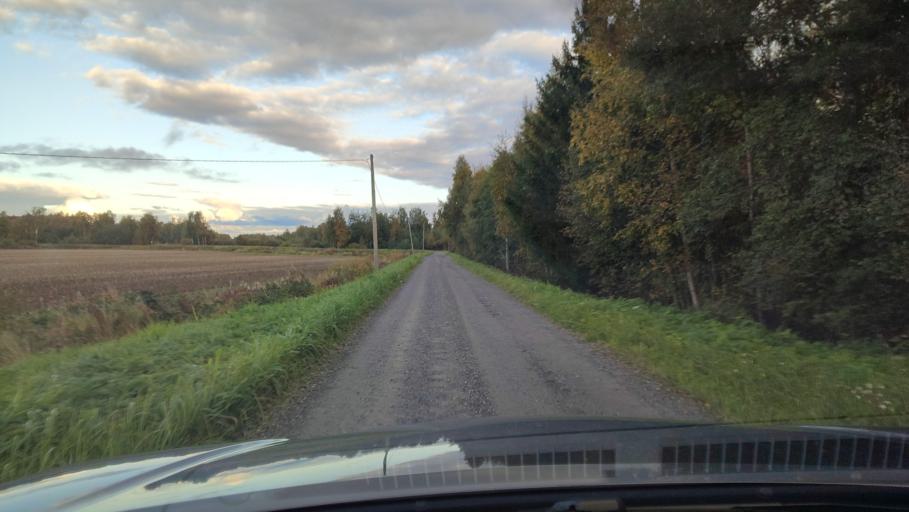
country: FI
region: Ostrobothnia
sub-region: Sydosterbotten
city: Kristinestad
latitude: 62.2315
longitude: 21.4443
